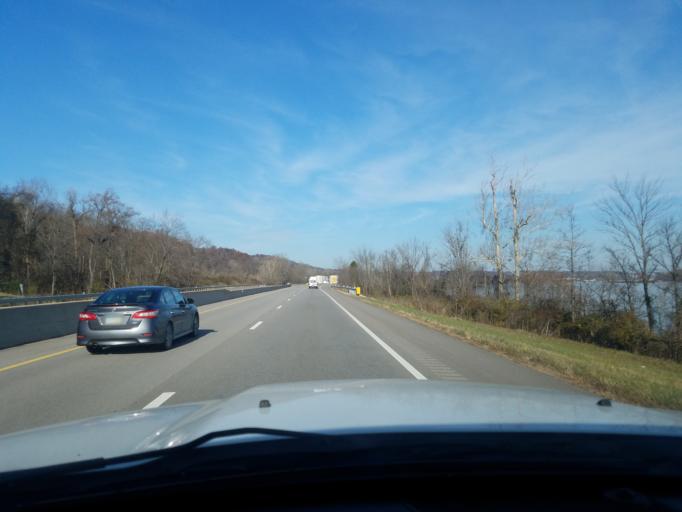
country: US
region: West Virginia
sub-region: Wood County
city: Vienna
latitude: 39.3371
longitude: -81.5601
